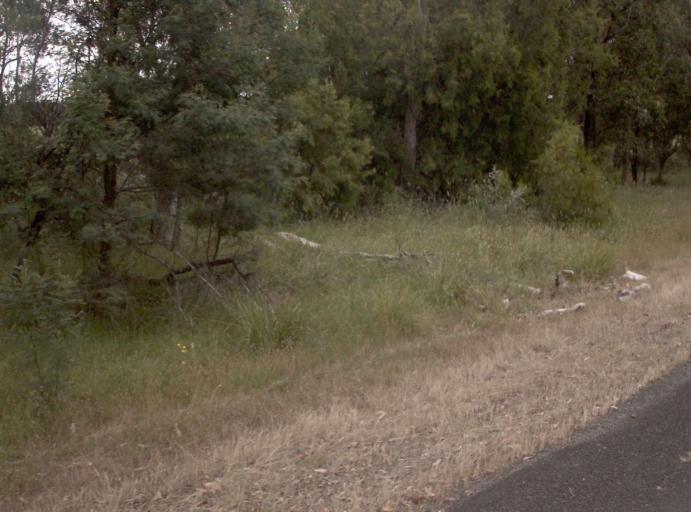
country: AU
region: Victoria
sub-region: Wellington
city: Sale
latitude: -38.3527
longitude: 146.9970
